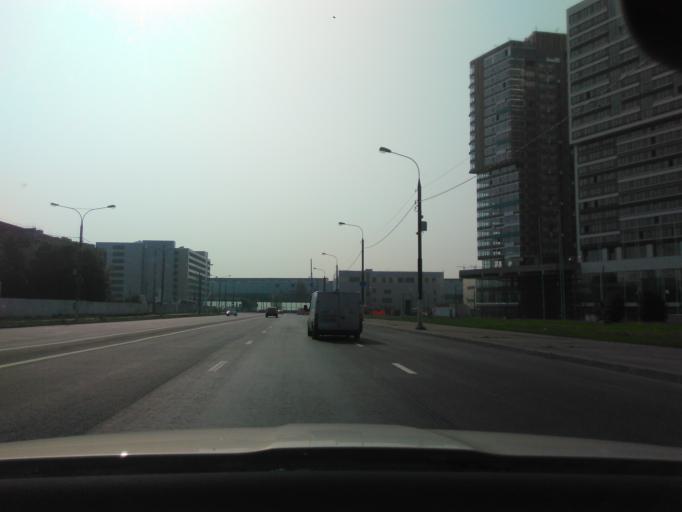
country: RU
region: Moscow
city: Sokol
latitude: 55.7886
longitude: 37.5416
